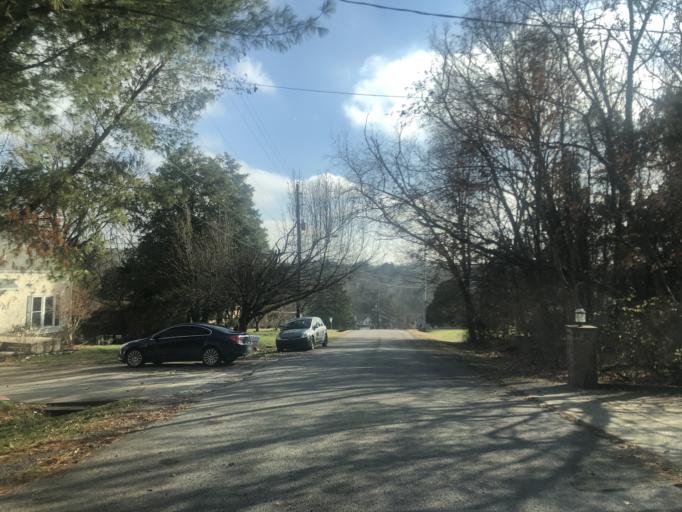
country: US
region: Tennessee
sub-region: Rutherford County
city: La Vergne
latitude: 36.0814
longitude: -86.6571
